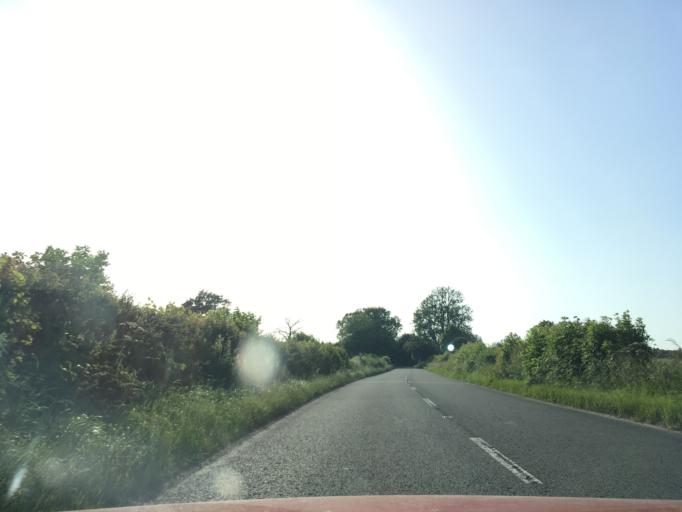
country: GB
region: England
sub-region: Wiltshire
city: Cricklade
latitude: 51.7096
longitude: -1.8676
